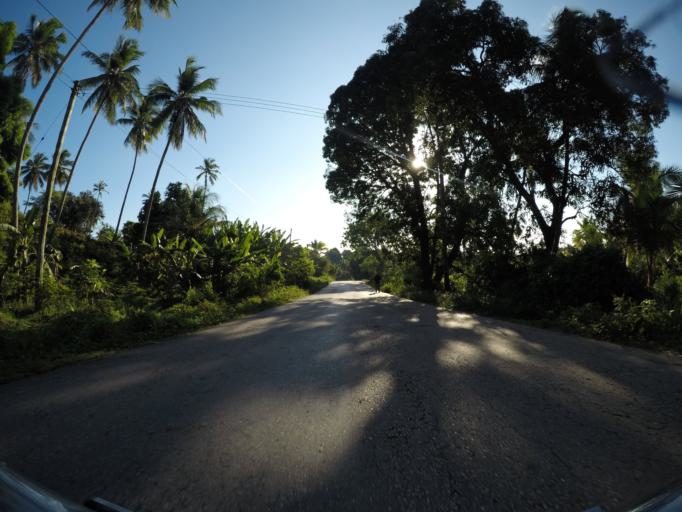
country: TZ
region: Pemba South
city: Mtambile
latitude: -5.3692
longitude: 39.7090
